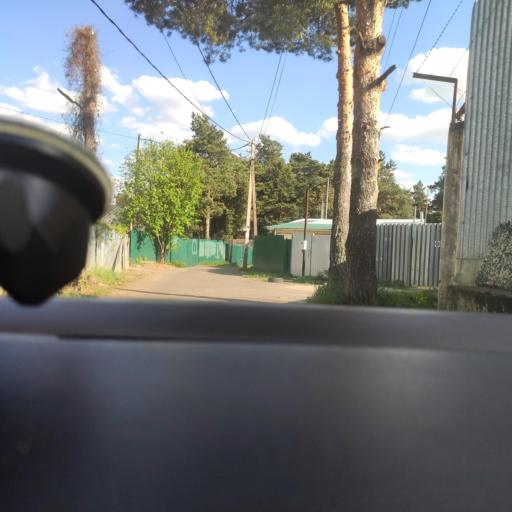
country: RU
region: Moskovskaya
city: Sheremet'yevskiy
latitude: 55.9959
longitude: 37.5444
